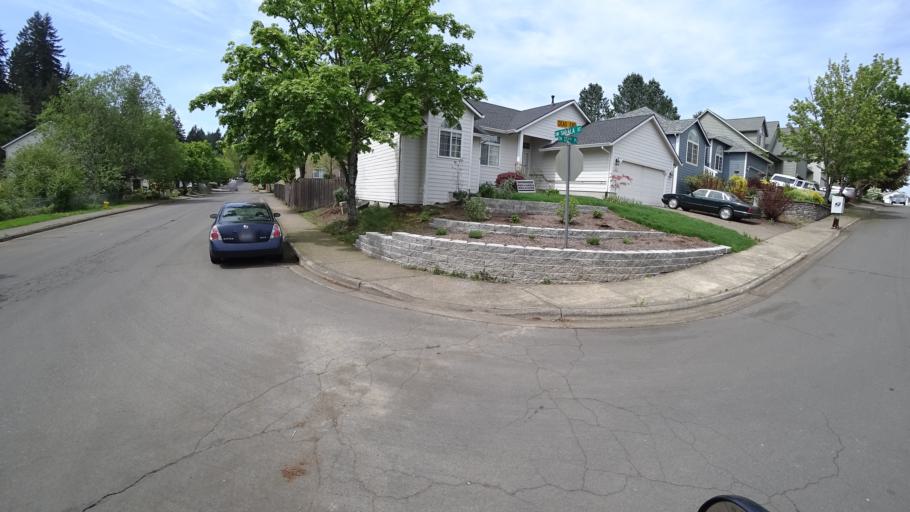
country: US
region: Oregon
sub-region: Washington County
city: Aloha
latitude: 45.4628
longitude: -122.8536
